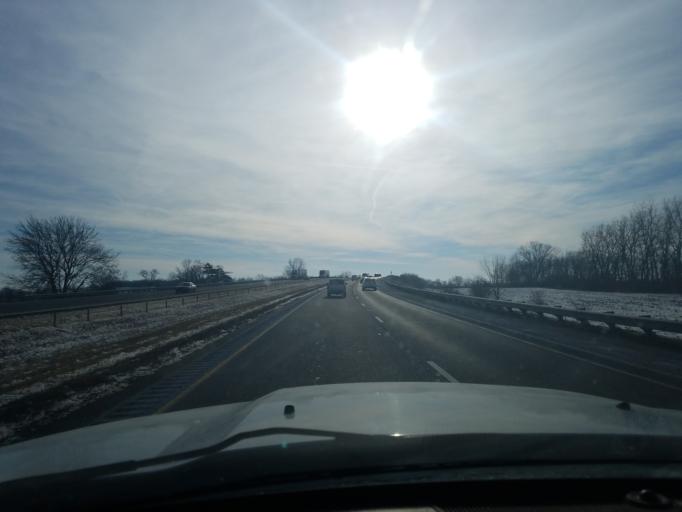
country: US
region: Indiana
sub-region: Grant County
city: Fairmount
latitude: 40.3820
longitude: -85.5507
